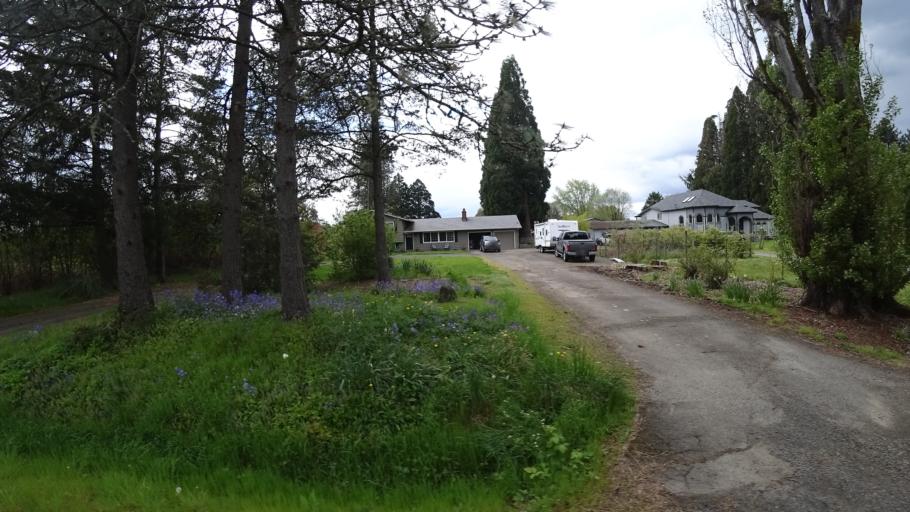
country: US
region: Oregon
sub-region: Washington County
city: Hillsboro
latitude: 45.5559
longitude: -122.9528
